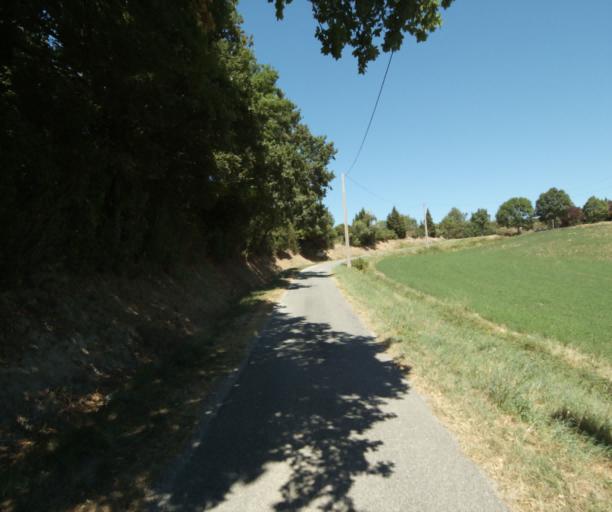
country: FR
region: Midi-Pyrenees
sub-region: Departement de la Haute-Garonne
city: Saint-Felix-Lauragais
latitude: 43.4920
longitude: 1.9277
